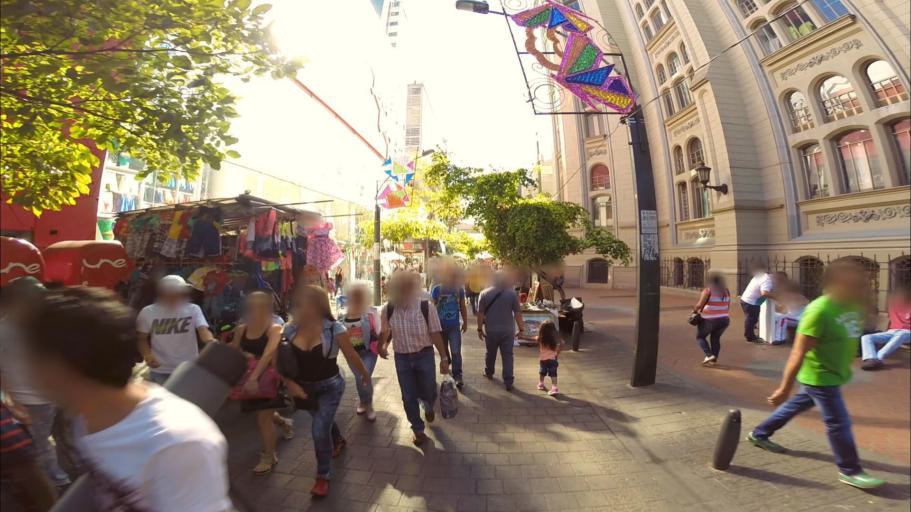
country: CO
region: Antioquia
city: Medellin
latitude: 6.2488
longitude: -75.5702
